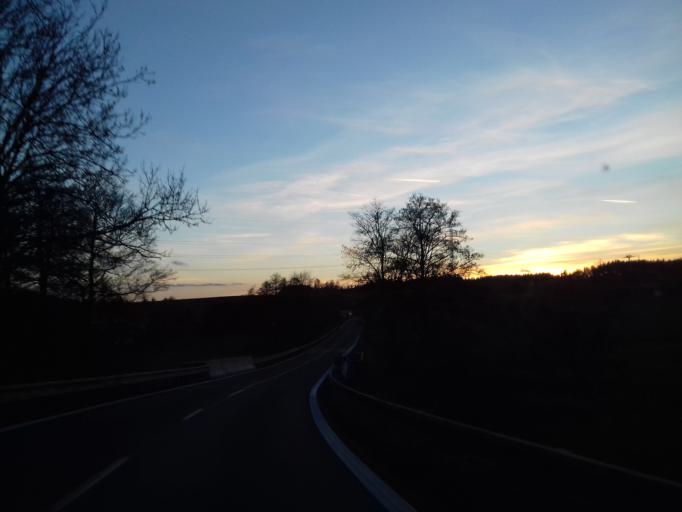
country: CZ
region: Vysocina
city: Chotebor
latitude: 49.6691
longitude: 15.7303
